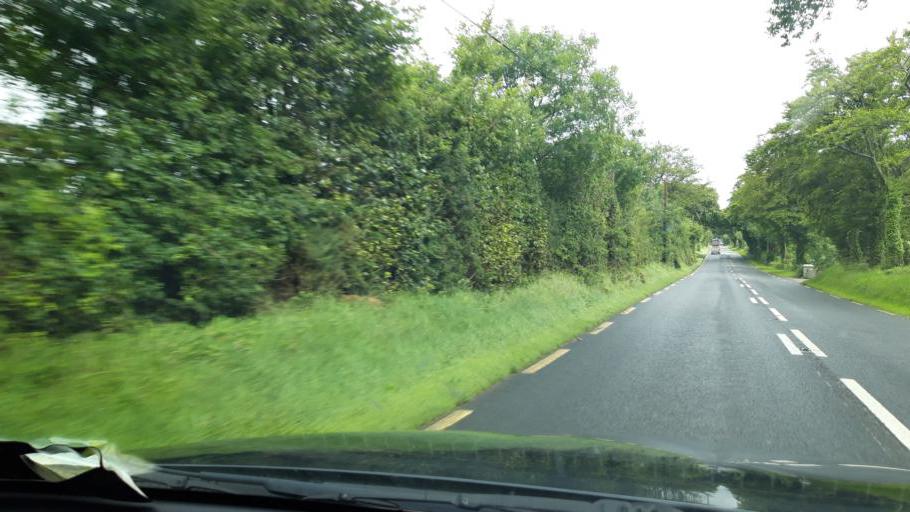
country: IE
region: Leinster
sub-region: Loch Garman
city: New Ross
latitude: 52.4335
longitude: -6.7707
